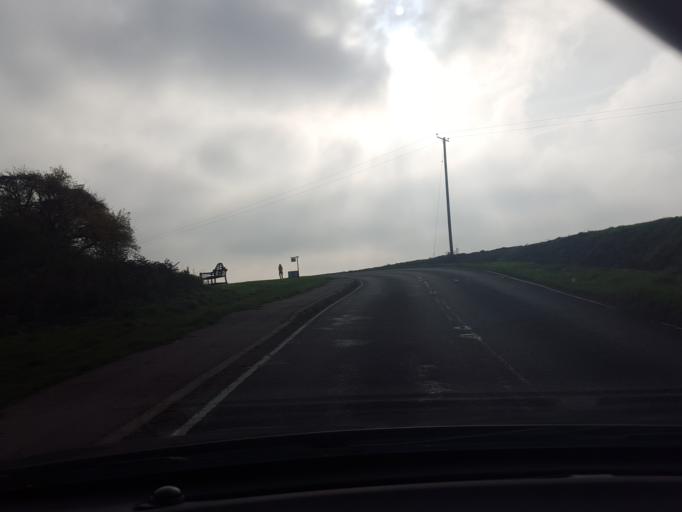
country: GB
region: England
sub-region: Essex
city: Mistley
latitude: 51.9387
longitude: 1.1126
